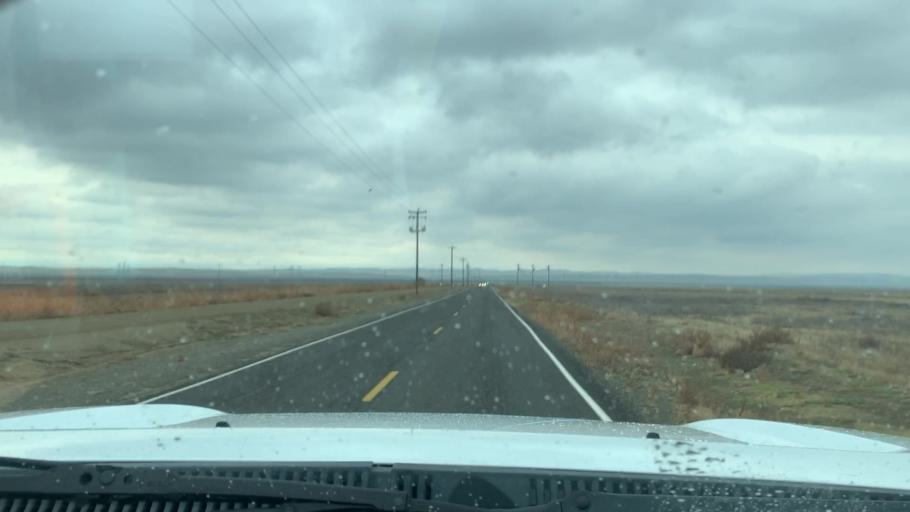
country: US
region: California
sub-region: Kings County
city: Kettleman City
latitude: 35.9343
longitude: -119.8746
